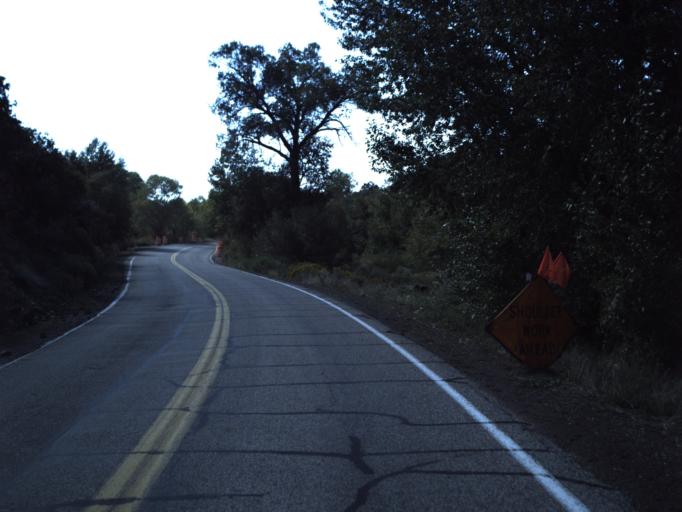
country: US
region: Utah
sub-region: Beaver County
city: Beaver
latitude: 38.2807
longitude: -112.5751
